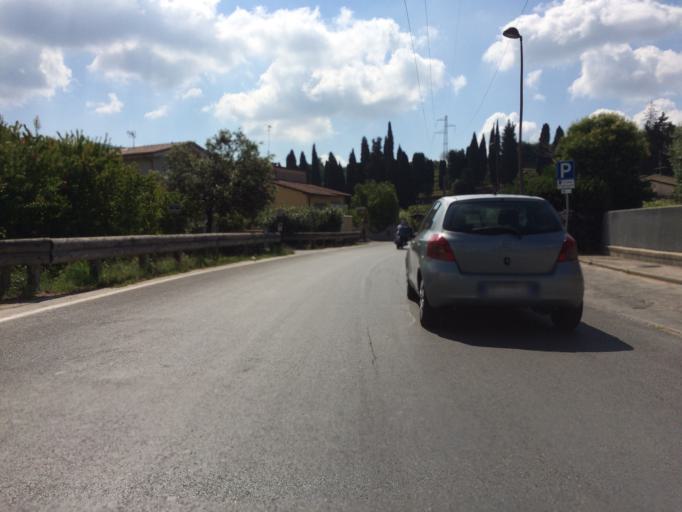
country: IT
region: Tuscany
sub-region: Provincia di Lucca
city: Massarosa
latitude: 43.8669
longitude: 10.3414
